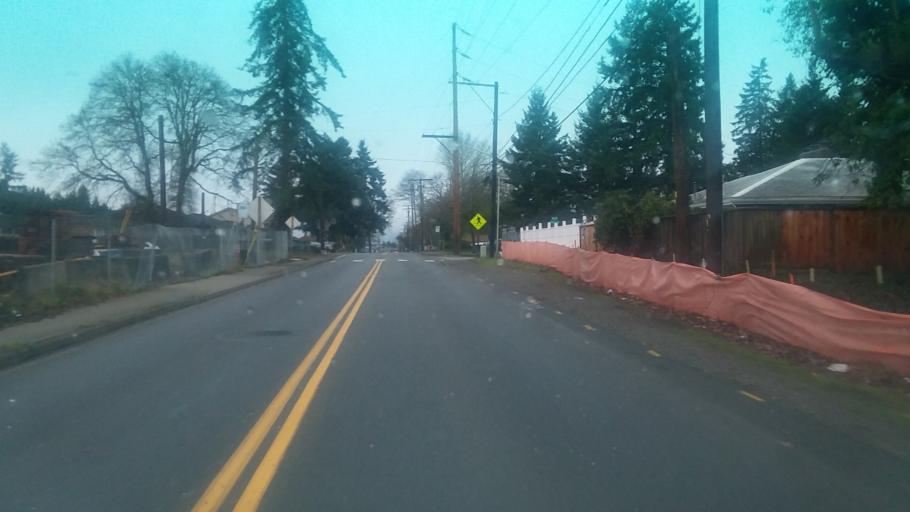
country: US
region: Washington
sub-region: Pierce County
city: Fort Lewis
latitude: 47.1270
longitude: -122.5448
